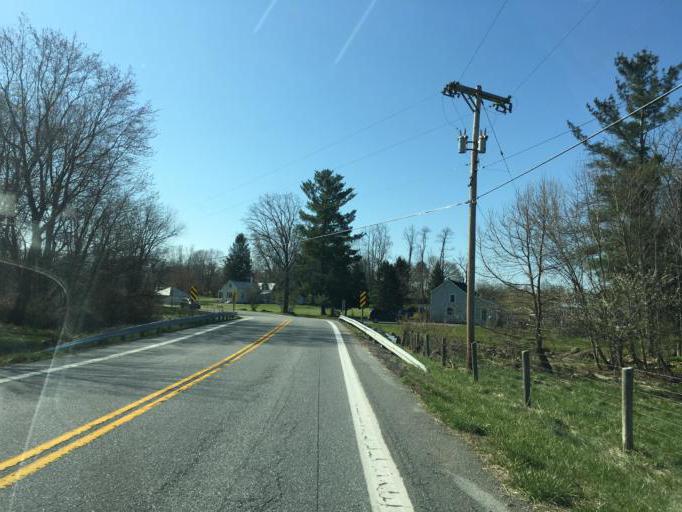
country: US
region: Maryland
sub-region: Washington County
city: Cavetown
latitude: 39.5793
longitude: -77.5564
